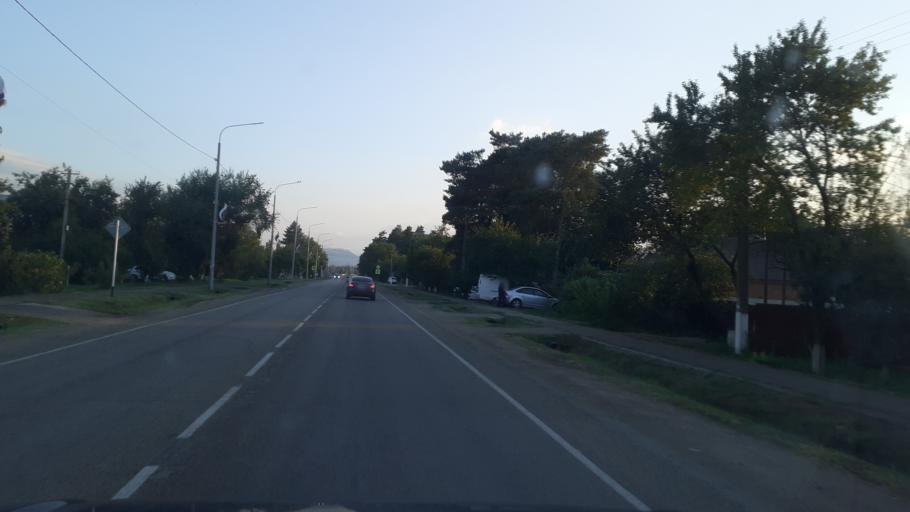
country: RU
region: Krasnodarskiy
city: Severskaya
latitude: 44.8369
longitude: 38.6675
